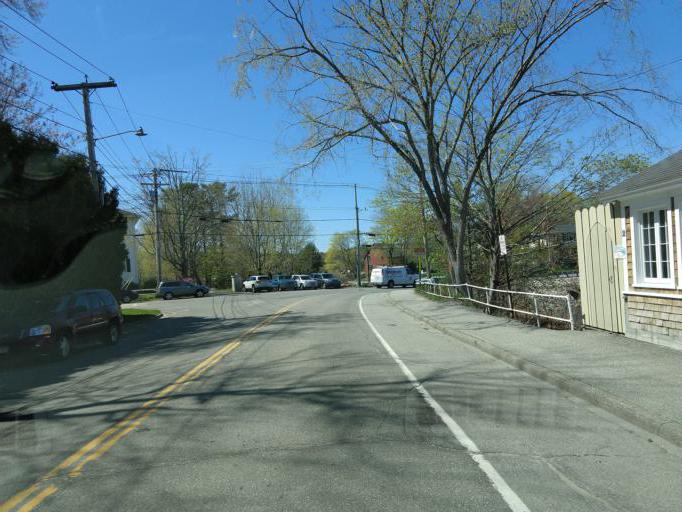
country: US
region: Maine
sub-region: York County
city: Kennebunkport
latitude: 43.3634
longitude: -70.4765
